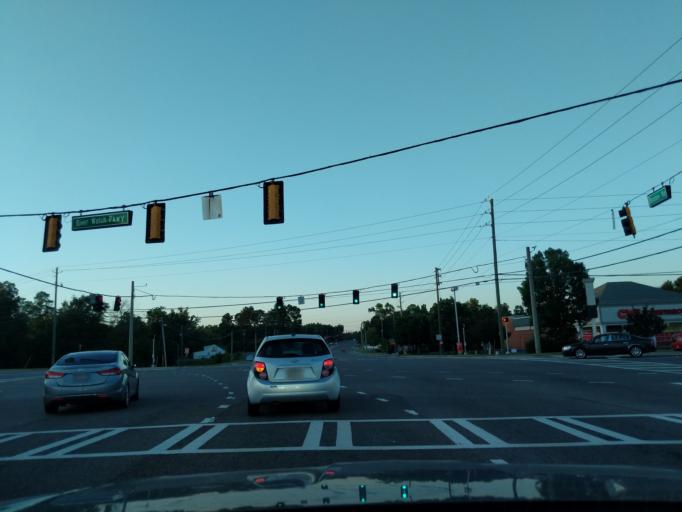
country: US
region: Georgia
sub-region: Columbia County
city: Martinez
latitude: 33.5175
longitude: -82.0772
